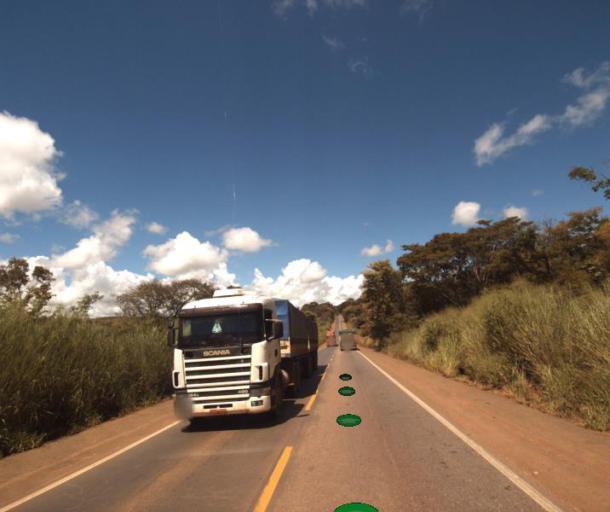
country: BR
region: Goias
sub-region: Anapolis
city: Anapolis
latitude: -16.1633
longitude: -49.0434
